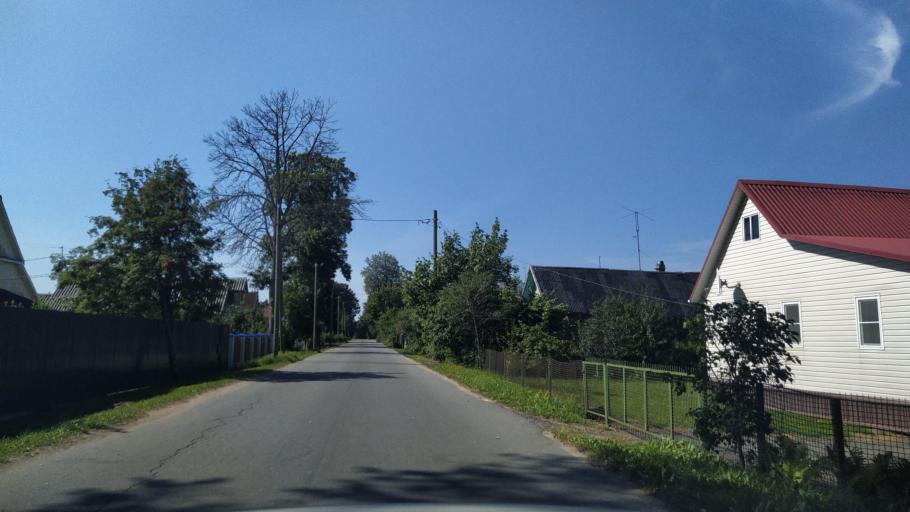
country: RU
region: Leningrad
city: Siverskiy
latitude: 59.2636
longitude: 30.0372
